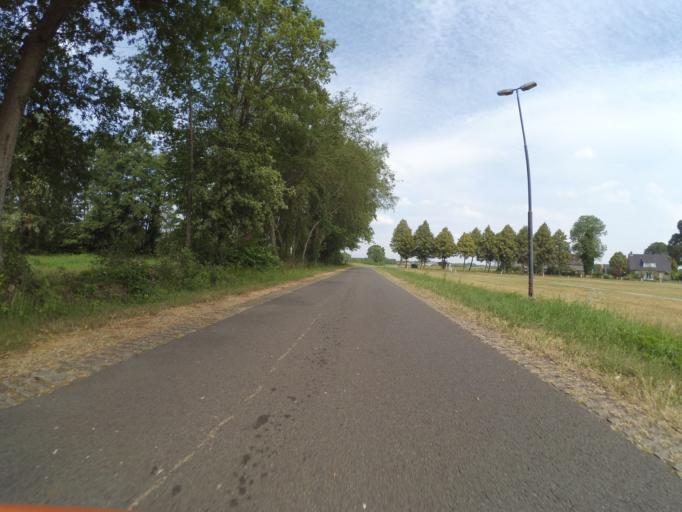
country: NL
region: Overijssel
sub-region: Gemeente Hof van Twente
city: Hengevelde
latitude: 52.1738
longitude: 6.6046
